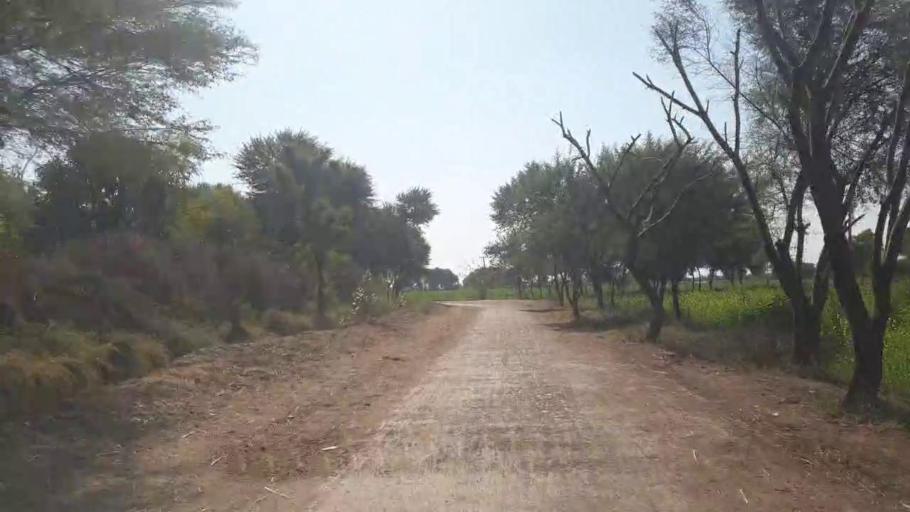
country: PK
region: Sindh
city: Chambar
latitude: 25.2914
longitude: 68.6860
